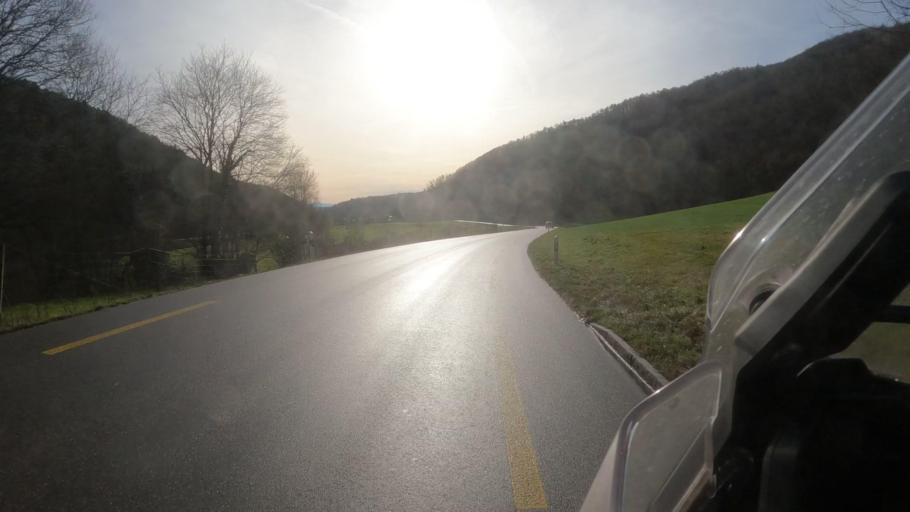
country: CH
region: Schaffhausen
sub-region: Bezirk Reiat
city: Stetten
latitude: 47.7454
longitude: 8.6180
